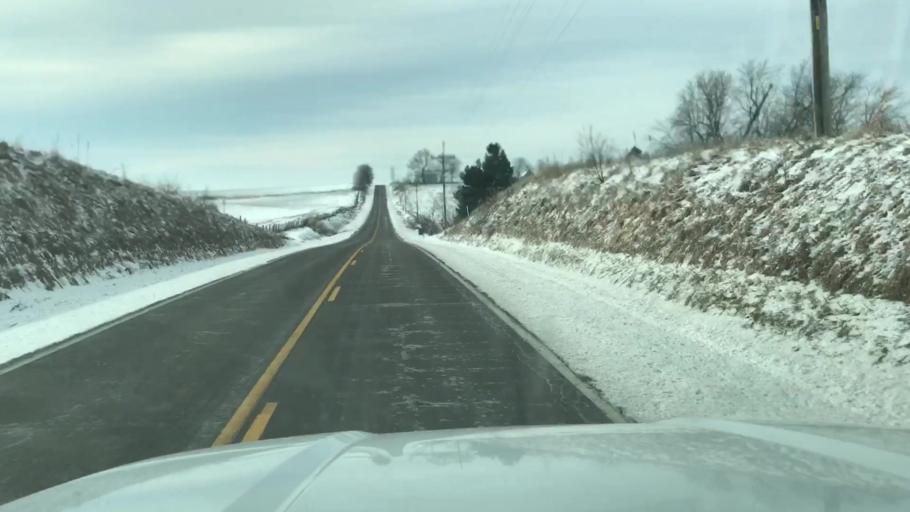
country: US
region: Missouri
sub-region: Holt County
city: Oregon
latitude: 40.0763
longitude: -95.1355
